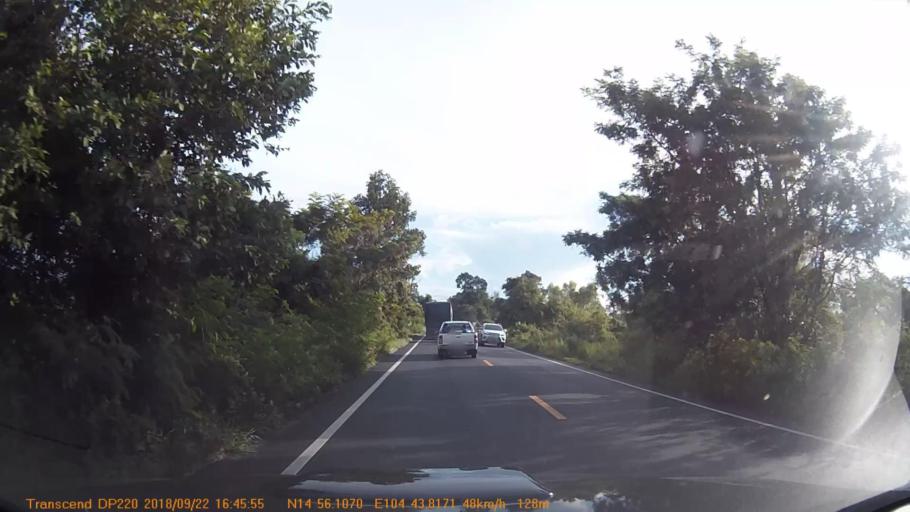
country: TH
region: Sisaket
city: Non Kho
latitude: 14.9350
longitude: 104.7302
